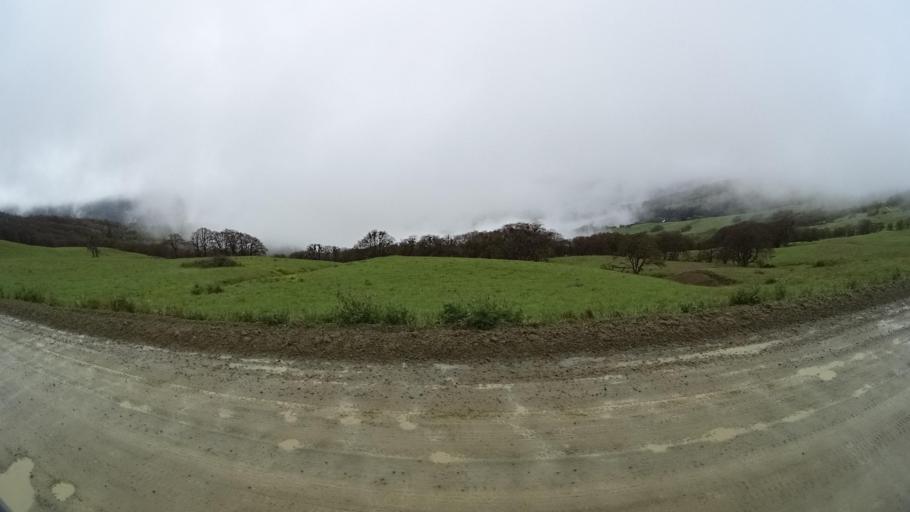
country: US
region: California
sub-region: Humboldt County
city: Westhaven-Moonstone
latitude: 41.1456
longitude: -123.8690
